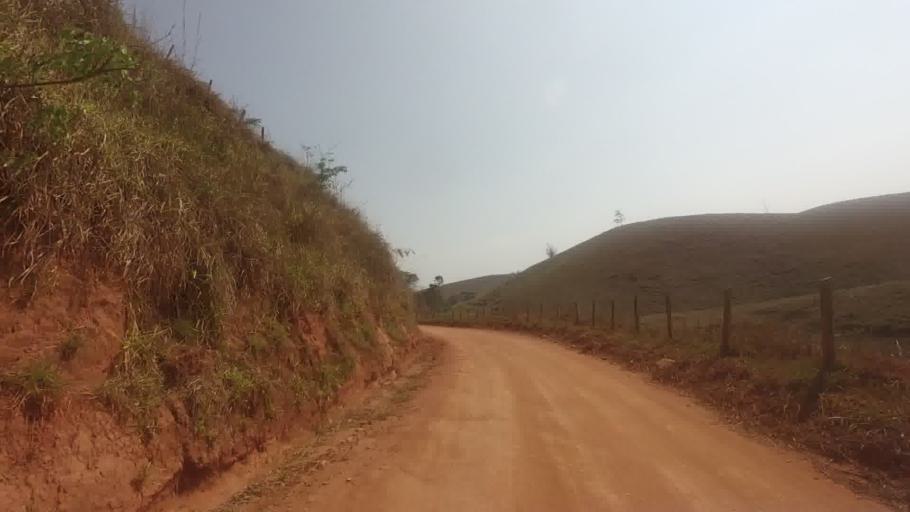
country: BR
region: Espirito Santo
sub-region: Sao Jose Do Calcado
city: Sao Jose do Calcado
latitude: -21.0664
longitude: -41.5468
